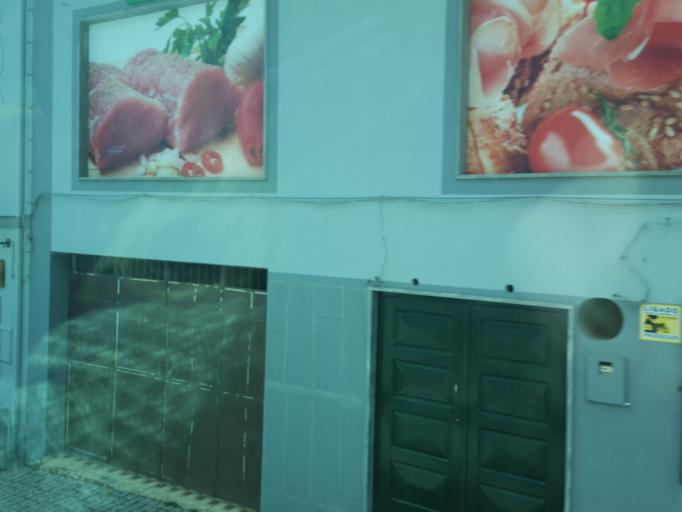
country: PT
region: Faro
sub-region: Monchique
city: Monchique
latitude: 37.3163
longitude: -8.5554
